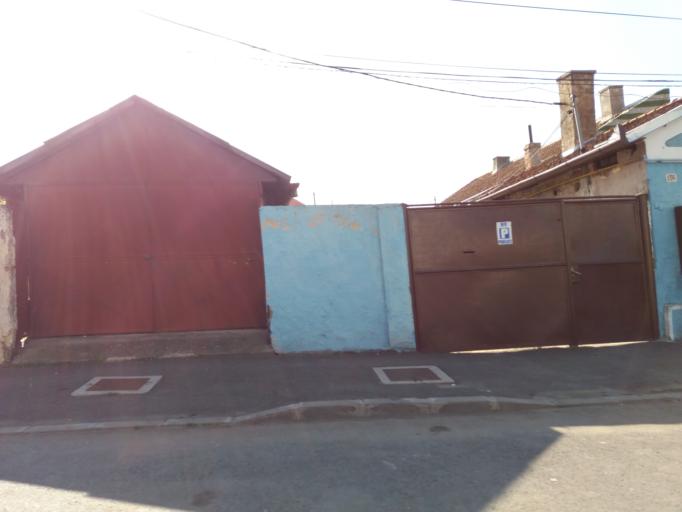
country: RO
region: Arad
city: Arad
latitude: 46.1698
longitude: 21.3035
